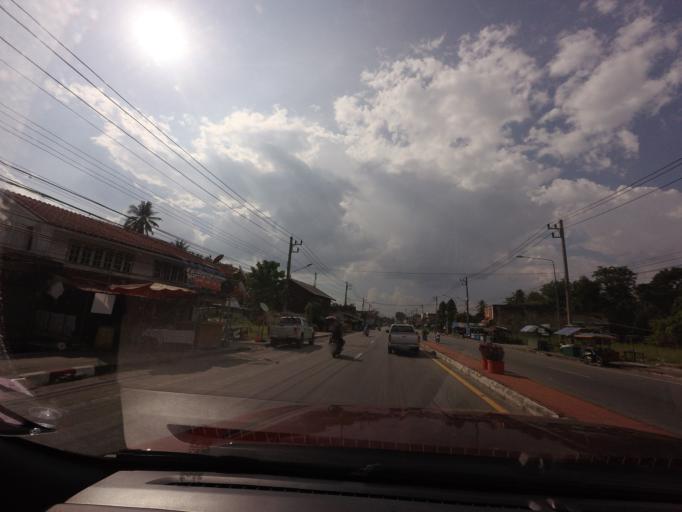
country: TH
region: Yala
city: Yala
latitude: 6.5774
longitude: 101.1987
